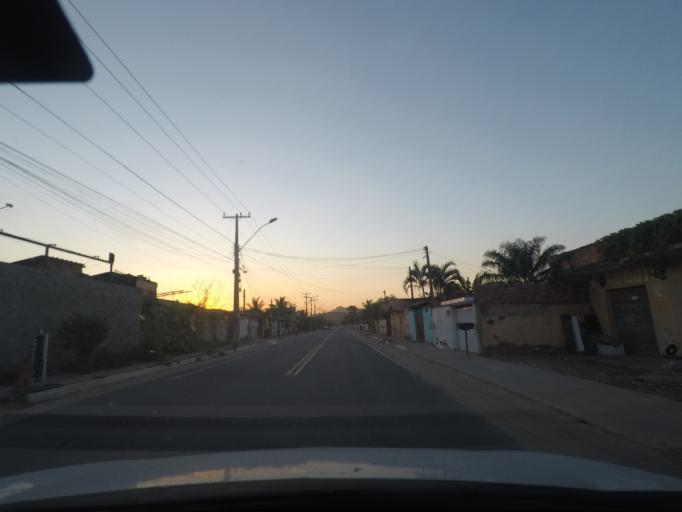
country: BR
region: Rio de Janeiro
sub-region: Marica
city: Marica
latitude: -22.9567
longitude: -42.9559
